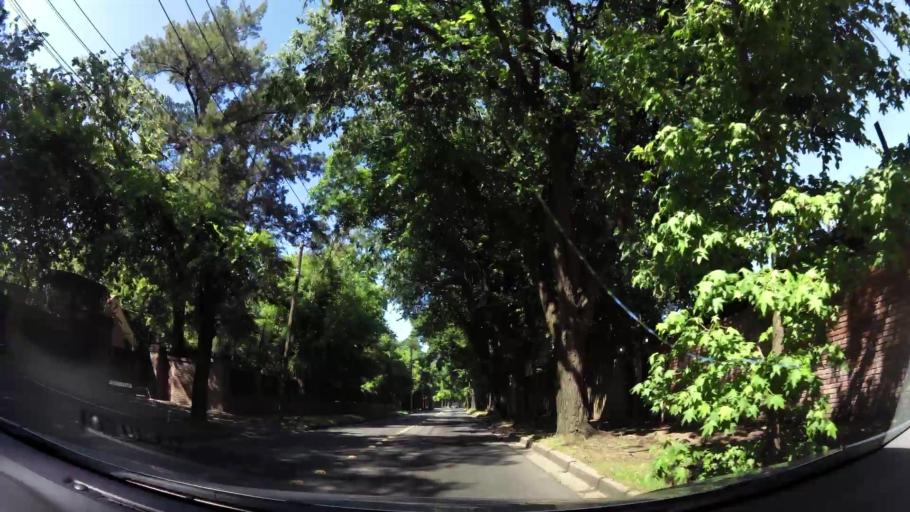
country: AR
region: Buenos Aires
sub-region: Partido de Tigre
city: Tigre
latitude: -34.4927
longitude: -58.5719
